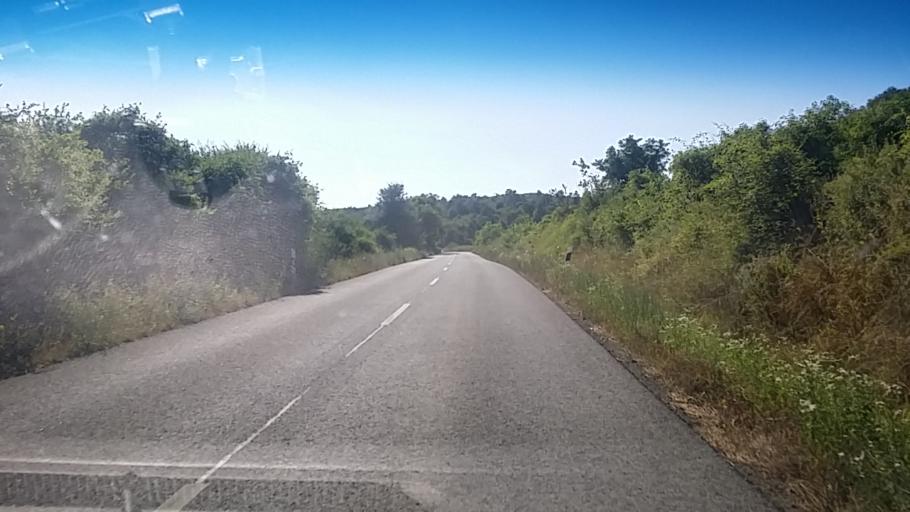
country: HU
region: Nograd
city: Romhany
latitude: 47.9220
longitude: 19.2124
